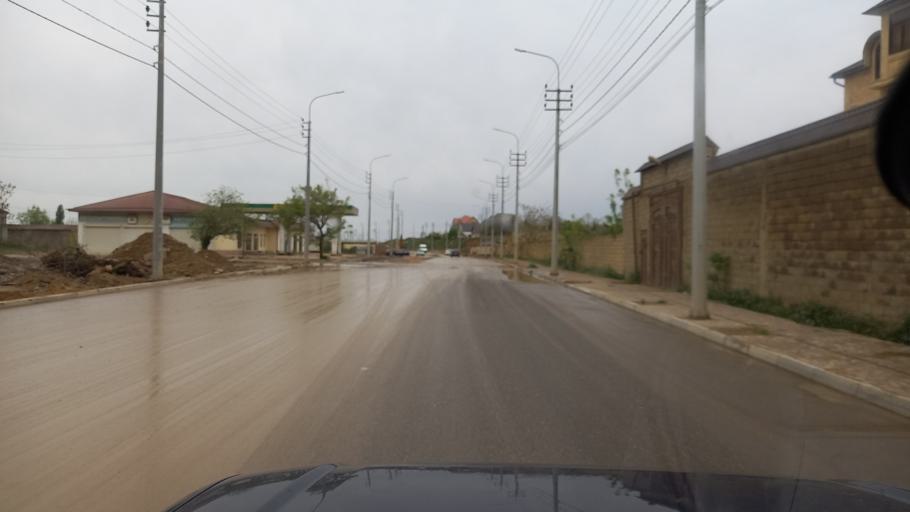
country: RU
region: Dagestan
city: Derbent
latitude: 42.0943
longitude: 48.2879
